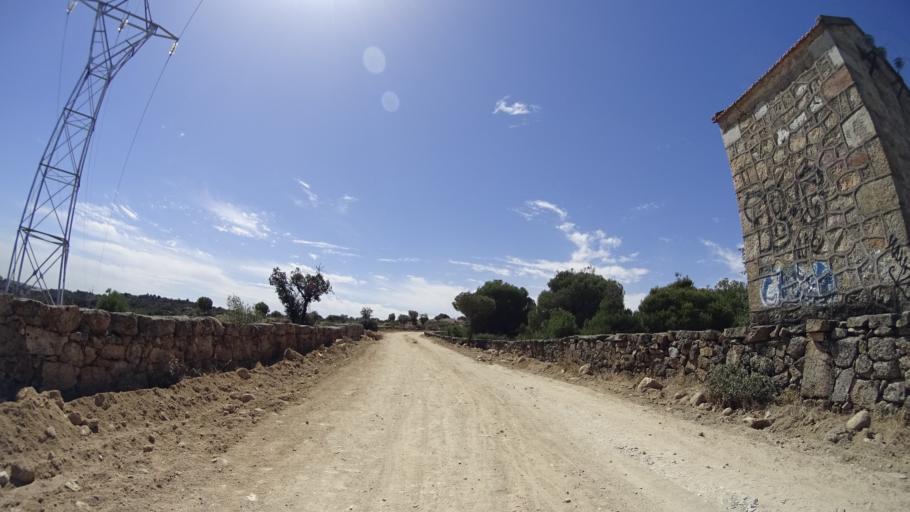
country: ES
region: Madrid
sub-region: Provincia de Madrid
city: Torrelodones
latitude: 40.5675
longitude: -3.9390
